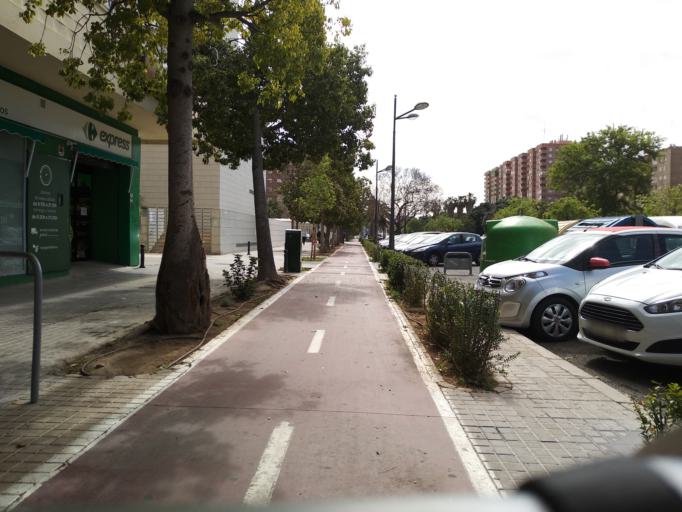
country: ES
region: Valencia
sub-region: Provincia de Valencia
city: Alboraya
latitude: 39.4717
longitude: -0.3390
